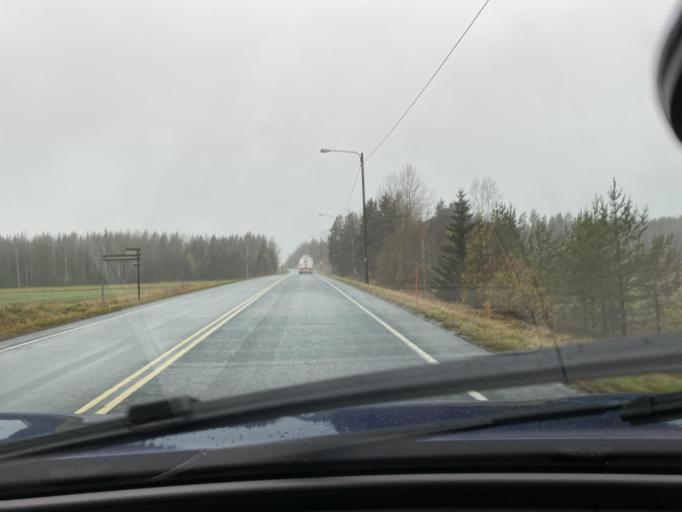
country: FI
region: Haeme
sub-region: Forssa
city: Ypaejae
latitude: 60.7747
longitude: 23.3633
